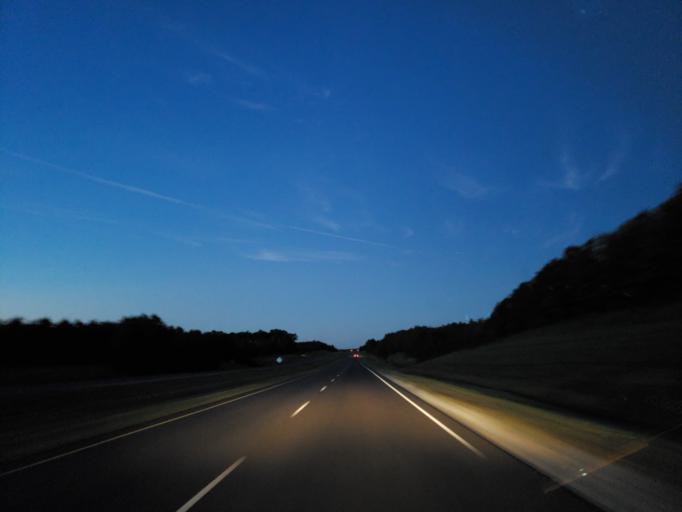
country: US
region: Mississippi
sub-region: Clarke County
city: Quitman
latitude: 32.0133
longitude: -88.6876
